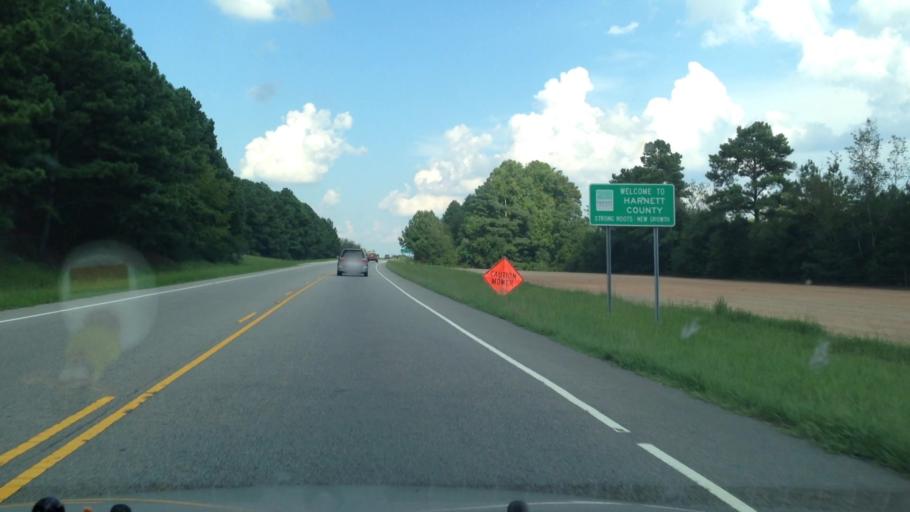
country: US
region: North Carolina
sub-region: Lee County
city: Broadway
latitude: 35.4390
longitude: -79.0481
